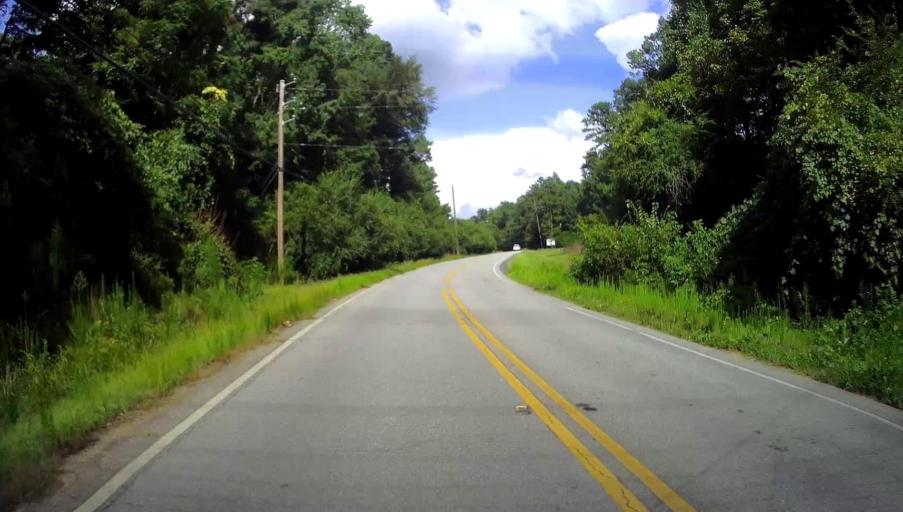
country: US
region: Georgia
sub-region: Muscogee County
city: Columbus
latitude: 32.5674
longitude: -84.8432
